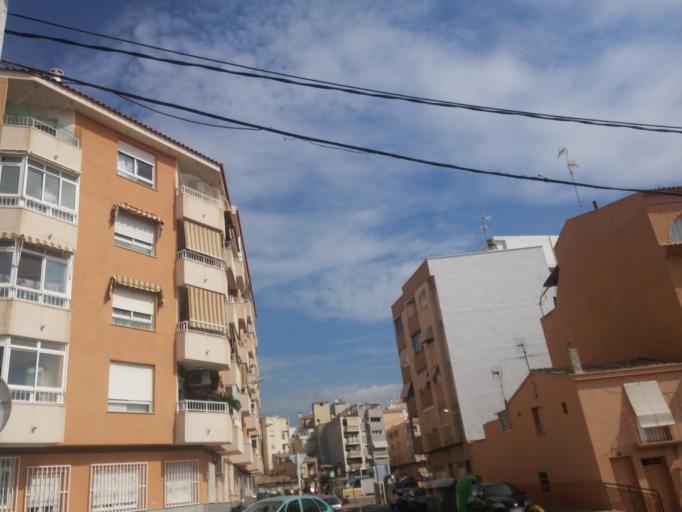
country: ES
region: Valencia
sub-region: Provincia de Alicante
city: Villajoyosa
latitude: 38.5038
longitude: -0.2356
